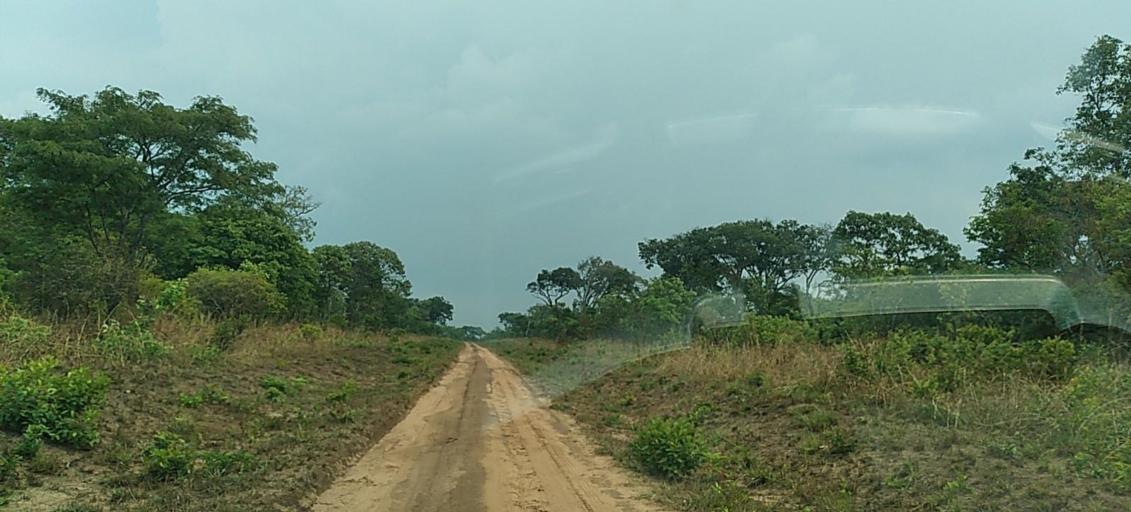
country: ZM
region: North-Western
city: Mwinilunga
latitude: -11.4373
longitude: 24.5940
